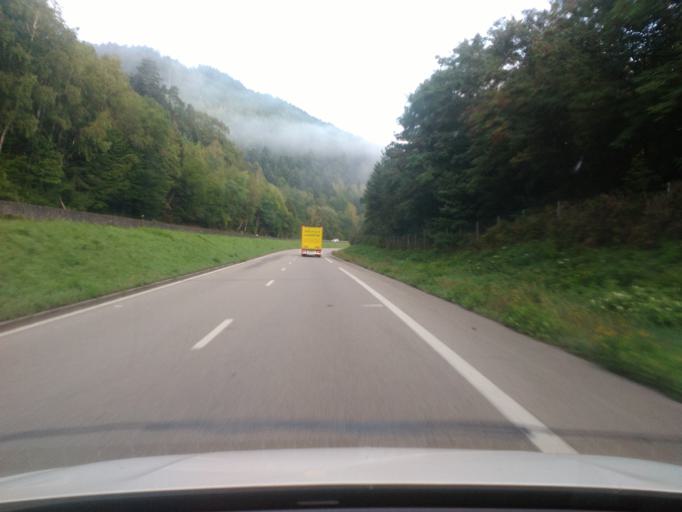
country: FR
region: Lorraine
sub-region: Departement des Vosges
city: Saint-Die-des-Vosges
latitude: 48.2765
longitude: 6.9426
